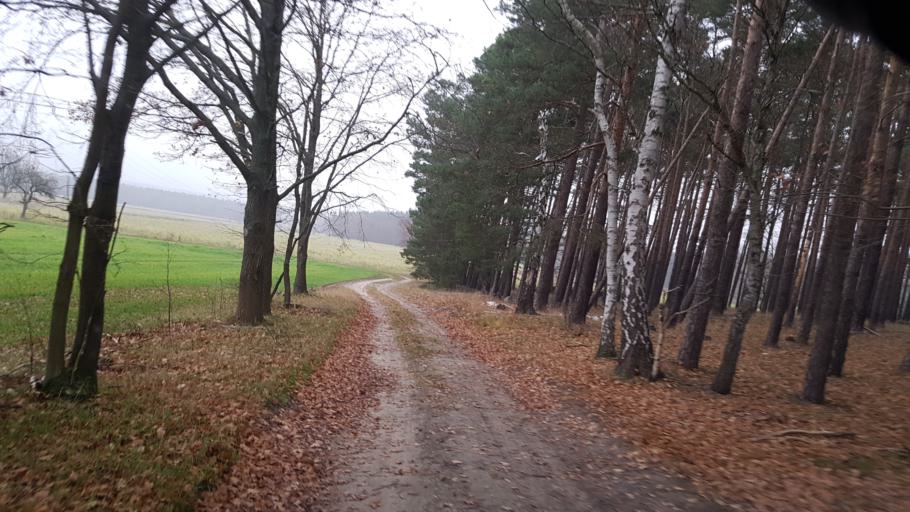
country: DE
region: Brandenburg
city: Altdobern
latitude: 51.6774
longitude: 13.9989
